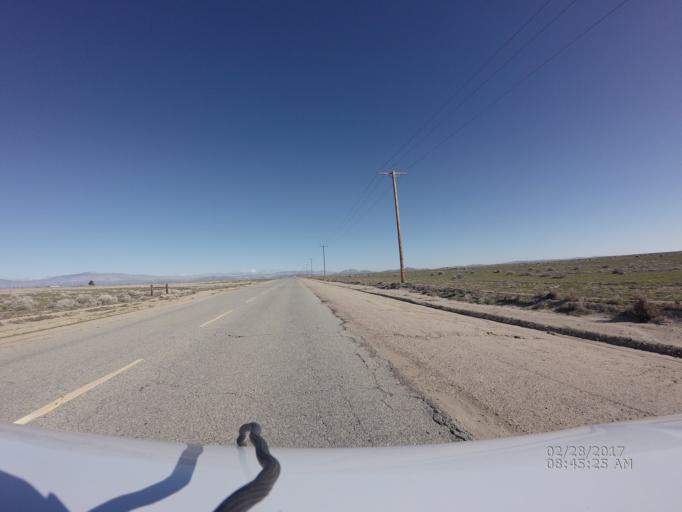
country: US
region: California
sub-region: Los Angeles County
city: Quartz Hill
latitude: 34.7637
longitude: -118.2372
